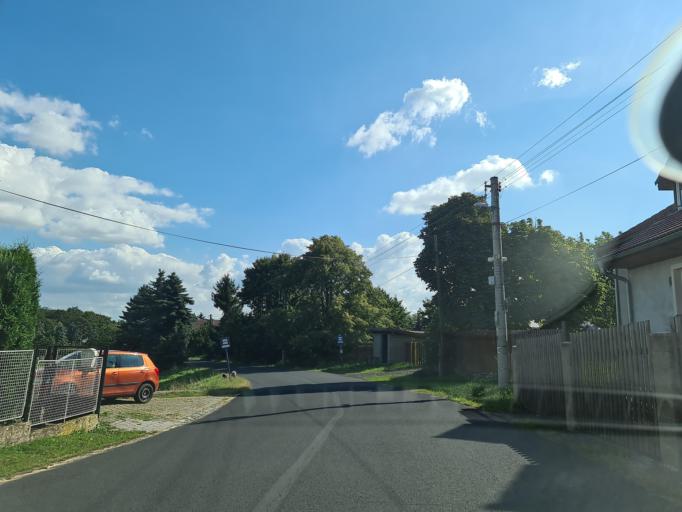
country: CZ
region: Ustecky
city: Horni Jiretin
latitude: 50.6040
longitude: 13.5550
